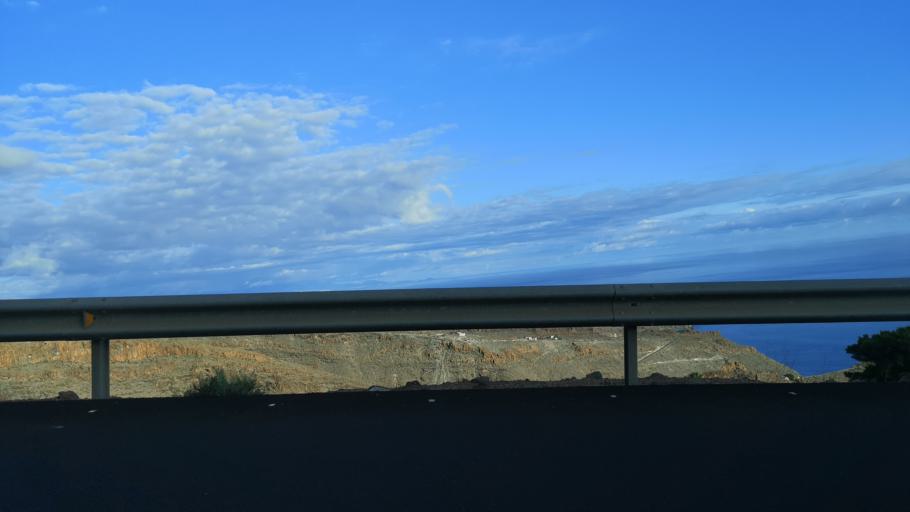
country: ES
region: Canary Islands
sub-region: Provincia de Santa Cruz de Tenerife
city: Alajero
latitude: 28.0445
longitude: -17.1932
